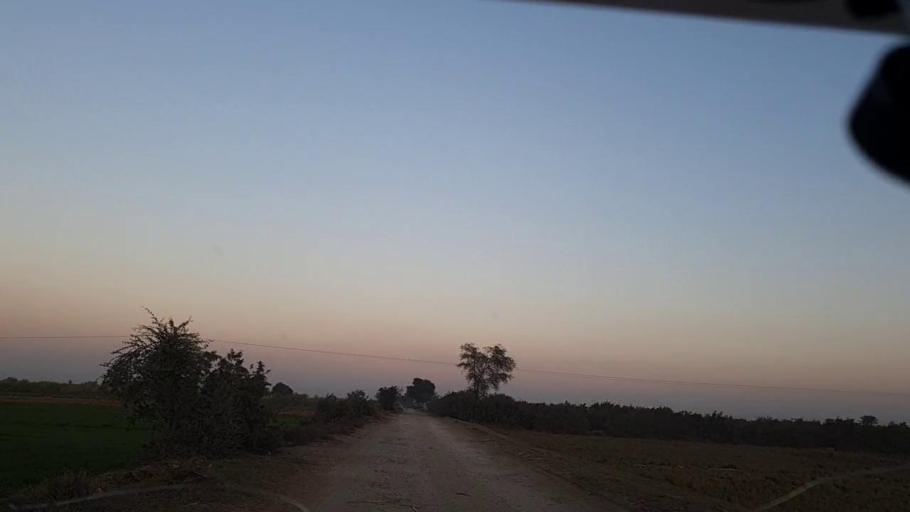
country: PK
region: Sindh
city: Adilpur
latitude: 27.8544
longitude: 69.2884
